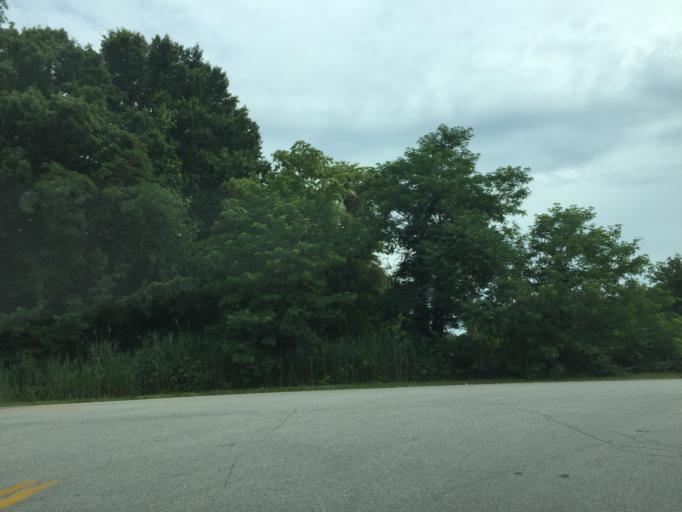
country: US
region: Maryland
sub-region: Baltimore County
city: Edgemere
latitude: 39.2725
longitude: -76.4609
